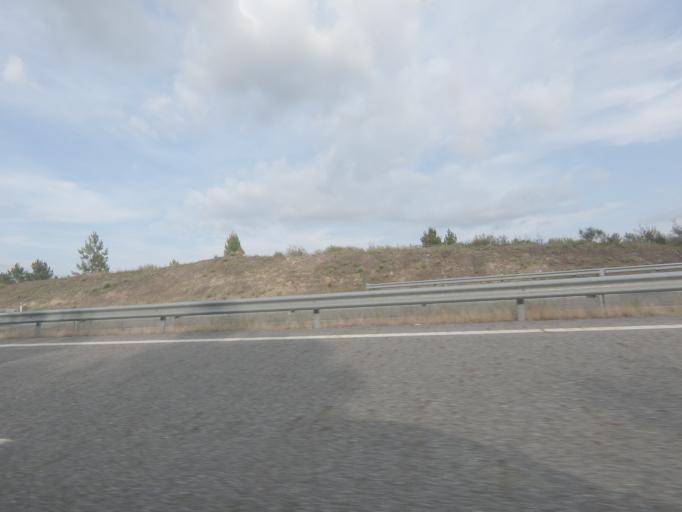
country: PT
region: Vila Real
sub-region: Chaves
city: Chaves
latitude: 41.6942
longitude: -7.5545
